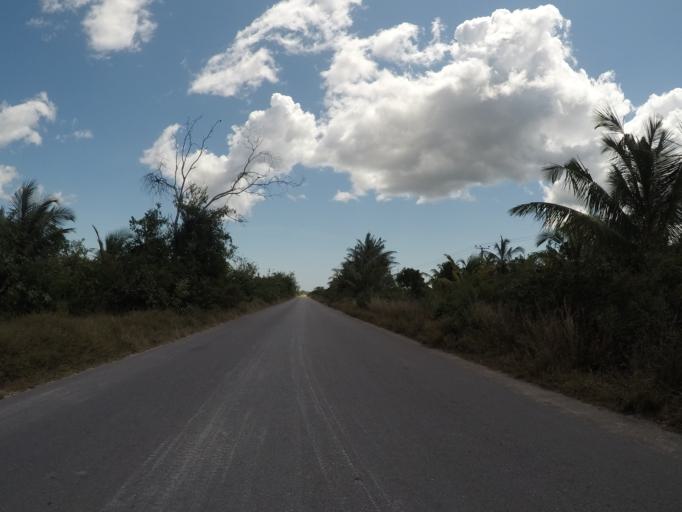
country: TZ
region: Zanzibar Central/South
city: Nganane
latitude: -6.2721
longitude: 39.4979
